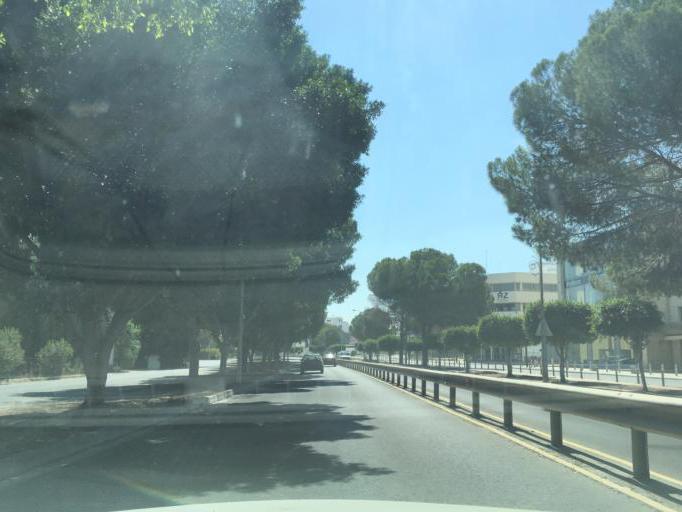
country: CY
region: Lefkosia
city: Nicosia
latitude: 35.1652
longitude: 33.3197
